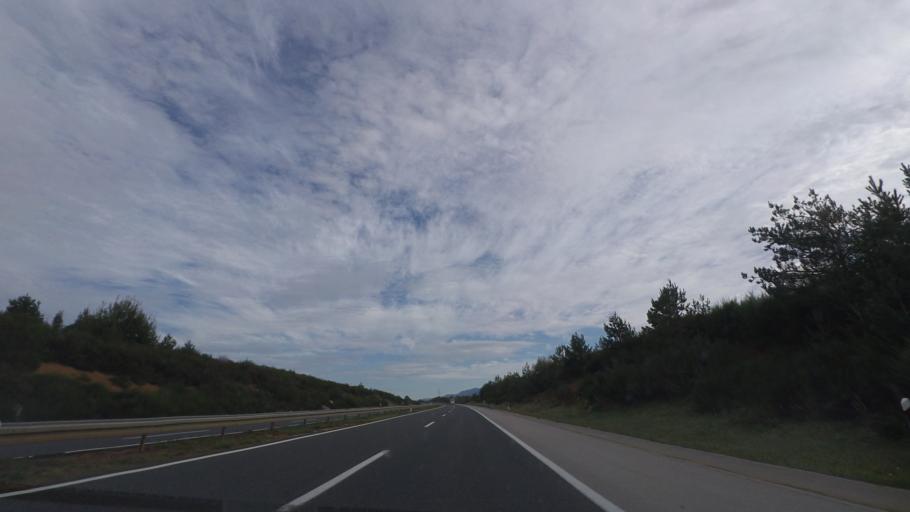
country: HR
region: Licko-Senjska
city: Gospic
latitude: 44.5394
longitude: 15.4393
